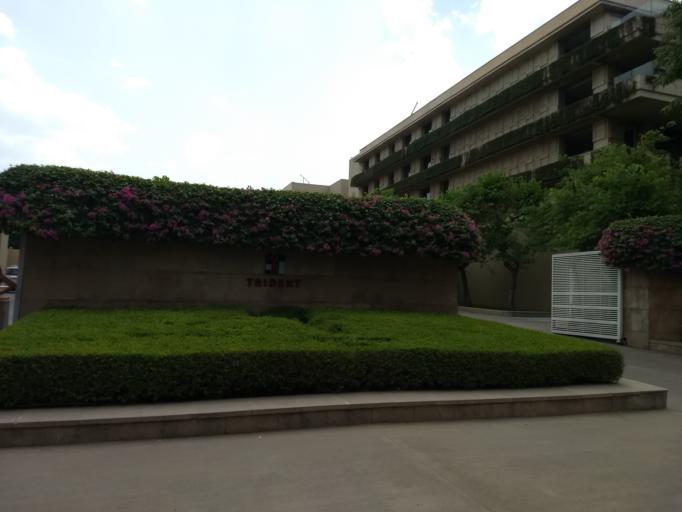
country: IN
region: Haryana
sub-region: Gurgaon
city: Gurgaon
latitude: 28.5024
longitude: 77.0894
